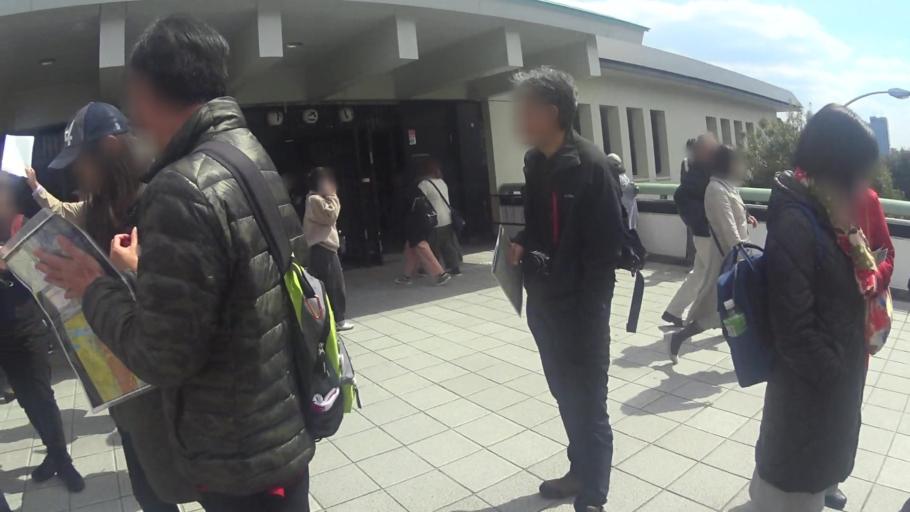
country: JP
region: Osaka
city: Osaka-shi
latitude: 34.6888
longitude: 135.5339
